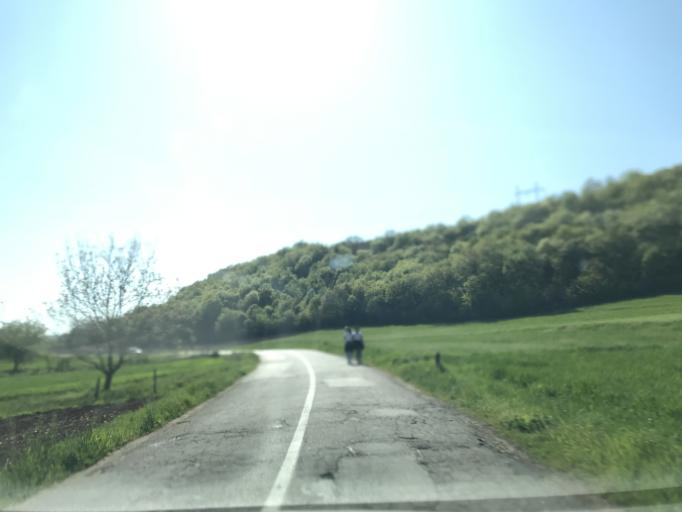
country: RS
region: Central Serbia
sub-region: Nisavski Okrug
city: Nis
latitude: 43.4094
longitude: 21.8120
